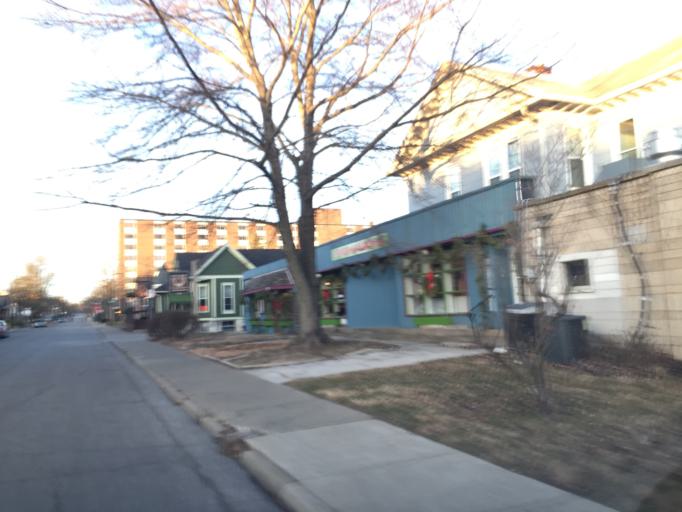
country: US
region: Indiana
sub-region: Monroe County
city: Bloomington
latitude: 39.1666
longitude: -86.5297
